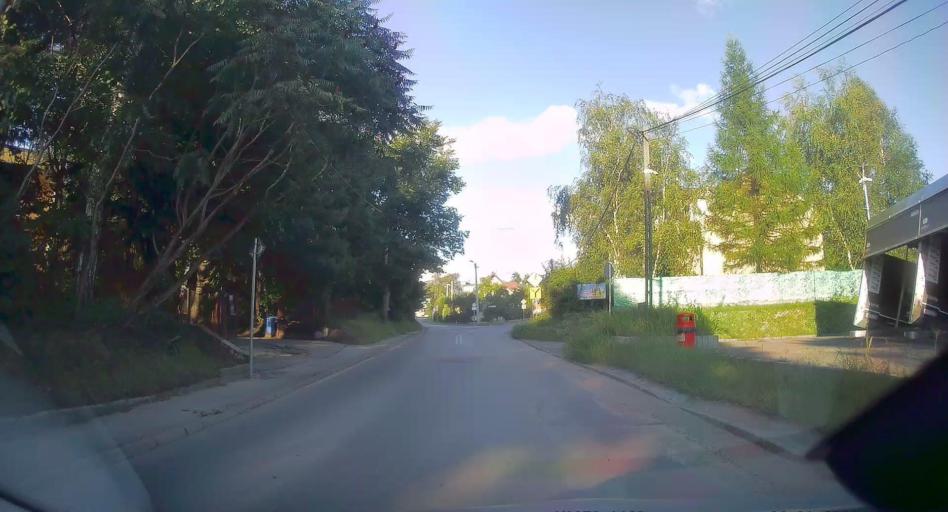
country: PL
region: Lesser Poland Voivodeship
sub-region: Powiat wielicki
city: Czarnochowice
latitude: 50.0157
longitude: 20.0531
